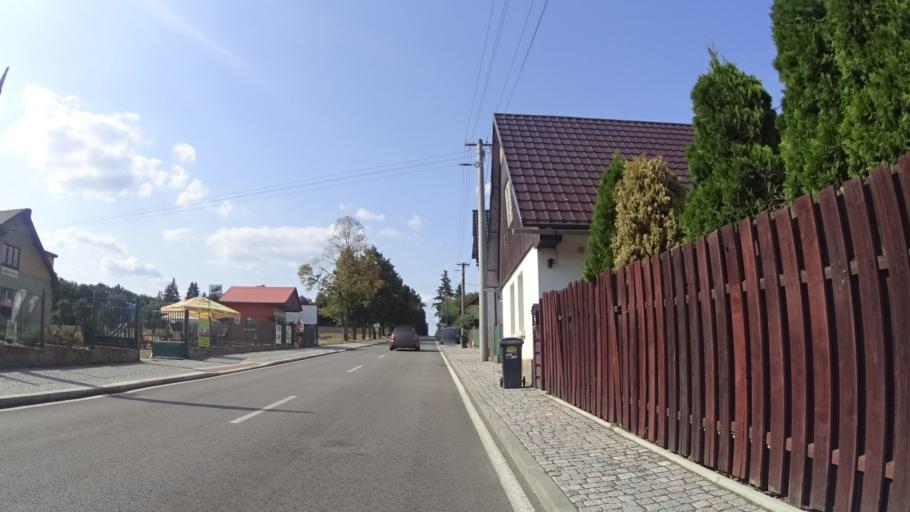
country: CZ
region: Kralovehradecky
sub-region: Okres Jicin
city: Sobotka
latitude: 50.4701
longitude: 15.1753
